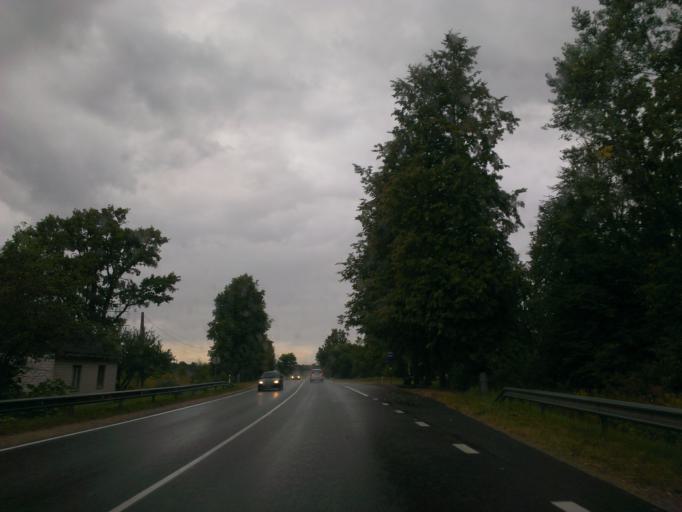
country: LV
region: Kegums
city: Kegums
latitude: 56.7588
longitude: 24.6966
